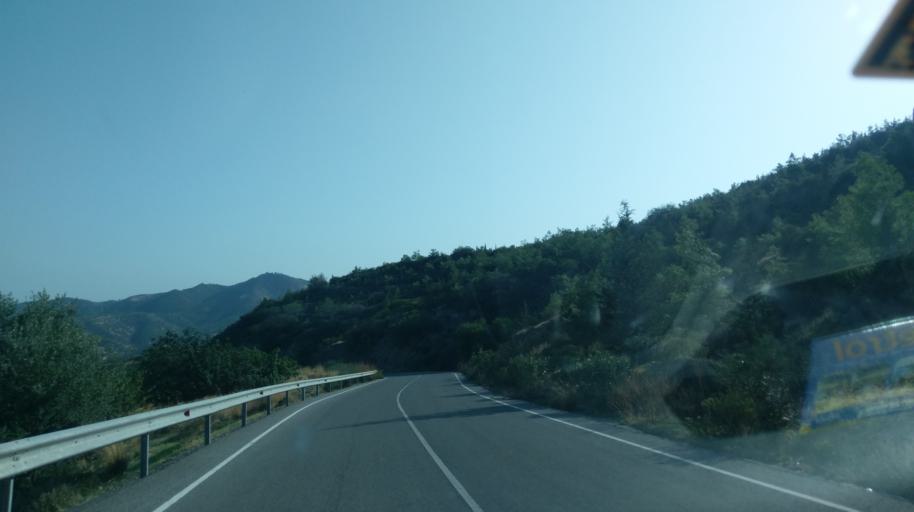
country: CY
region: Lefkosia
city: Kato Pyrgos
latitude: 35.1713
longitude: 32.7253
